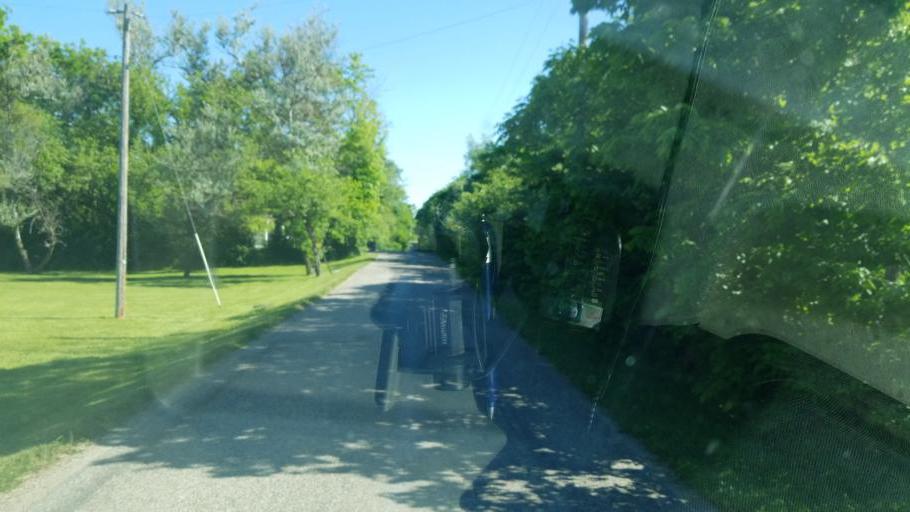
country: US
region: Ohio
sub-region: Preble County
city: New Paris
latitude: 39.8694
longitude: -84.8323
